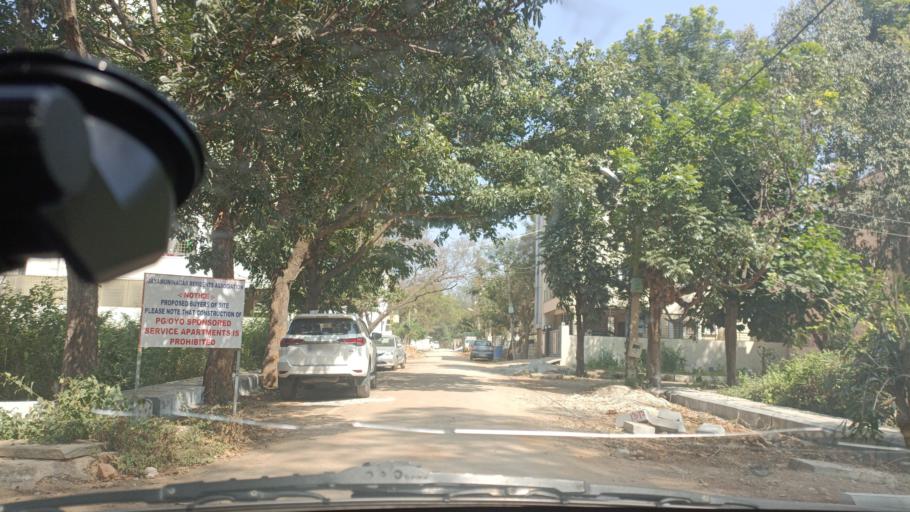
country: IN
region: Karnataka
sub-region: Bangalore Urban
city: Yelahanka
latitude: 13.1217
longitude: 77.6081
